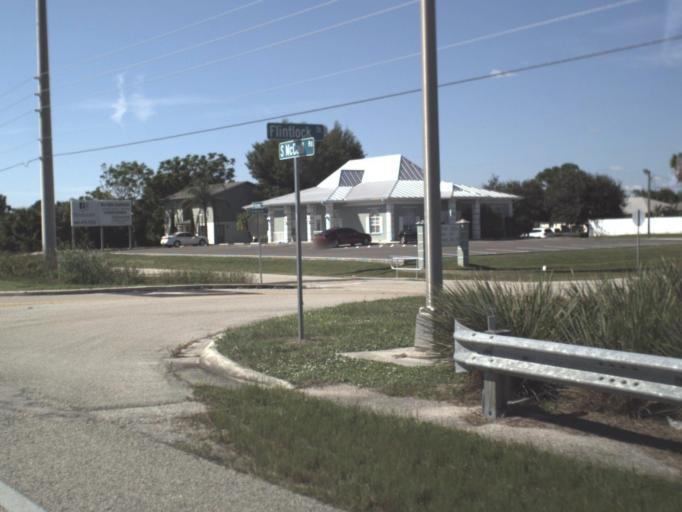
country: US
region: Florida
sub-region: Charlotte County
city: Rotonda
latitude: 26.9329
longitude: -82.2773
